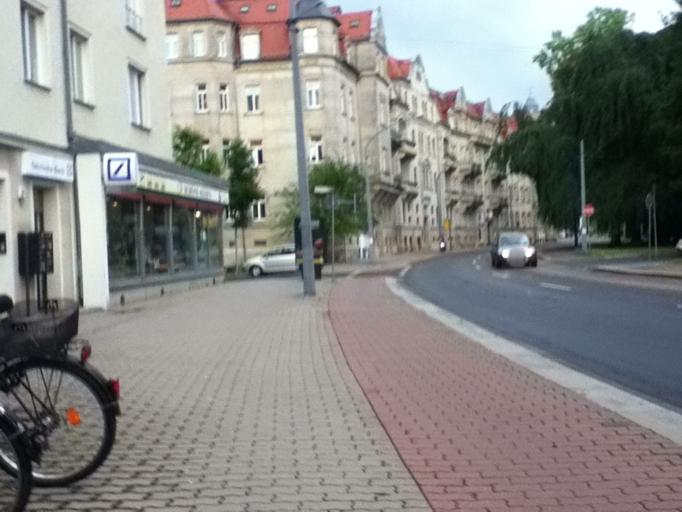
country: DE
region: Saxony
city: Dresden
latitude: 51.0342
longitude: 13.7223
